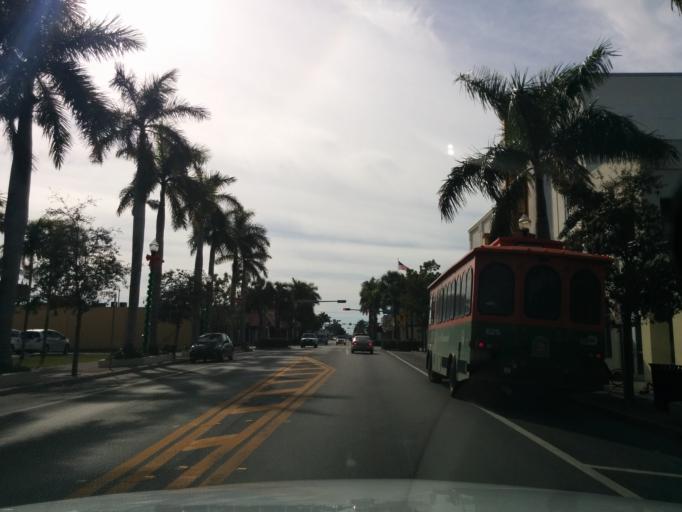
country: US
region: Florida
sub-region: Miami-Dade County
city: Homestead
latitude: 25.4706
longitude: -80.4774
